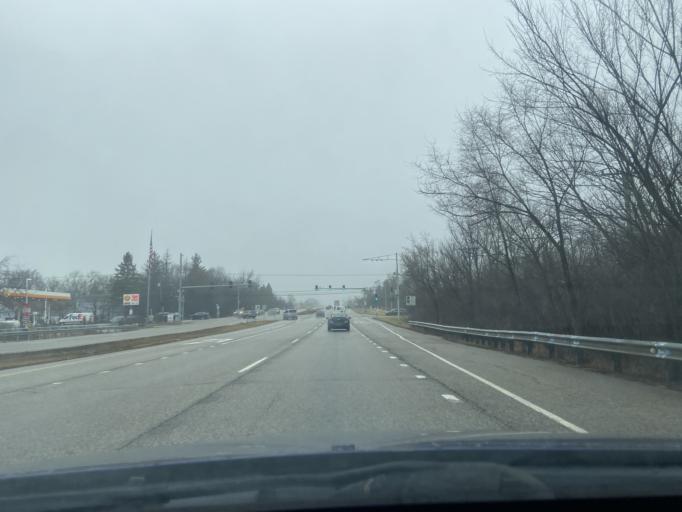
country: US
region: Illinois
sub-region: Lake County
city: Knollwood
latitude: 42.2111
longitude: -88.1114
